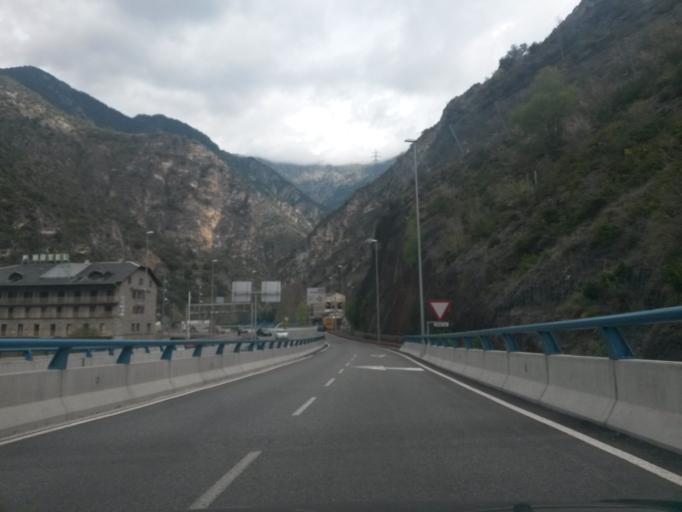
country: AD
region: Sant Julia de Loria
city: Sant Julia de Loria
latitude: 42.4752
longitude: 1.4909
